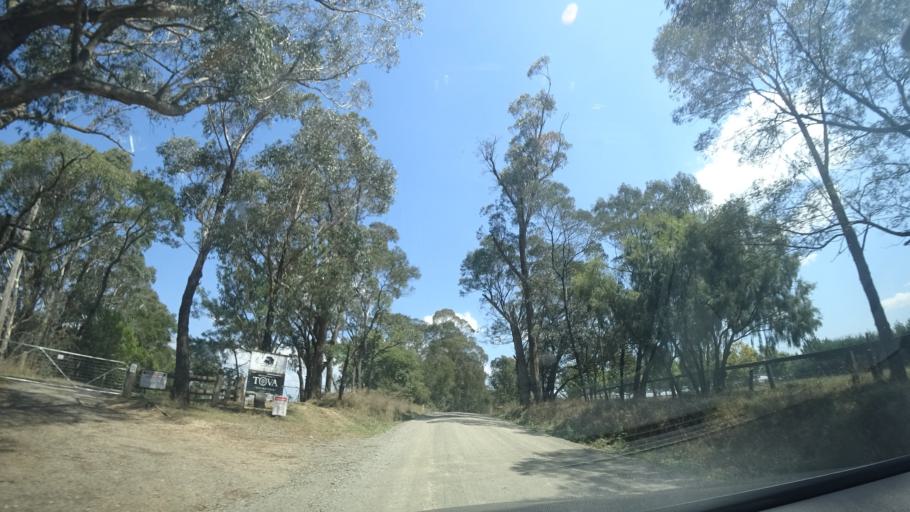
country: AU
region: New South Wales
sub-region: Wingecarribee
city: Bundanoon
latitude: -34.6216
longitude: 150.2704
